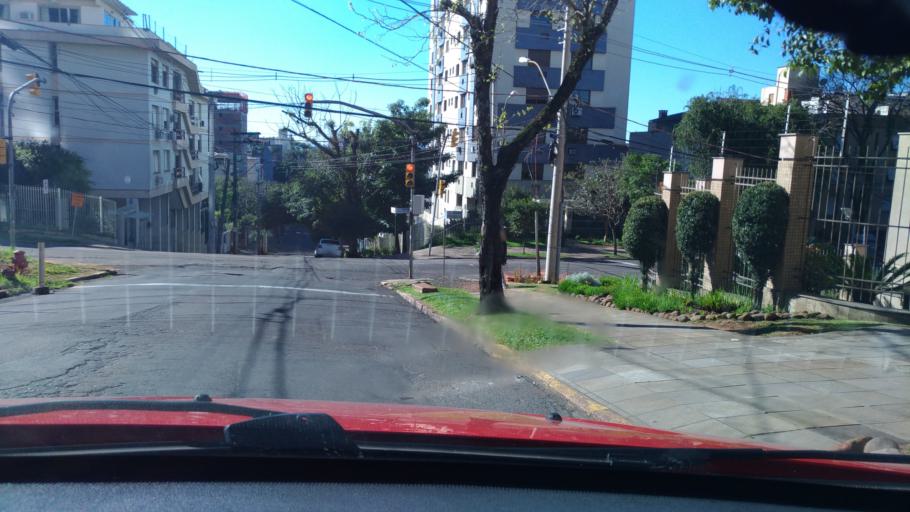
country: BR
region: Rio Grande do Sul
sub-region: Porto Alegre
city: Porto Alegre
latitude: -30.0174
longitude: -51.1841
